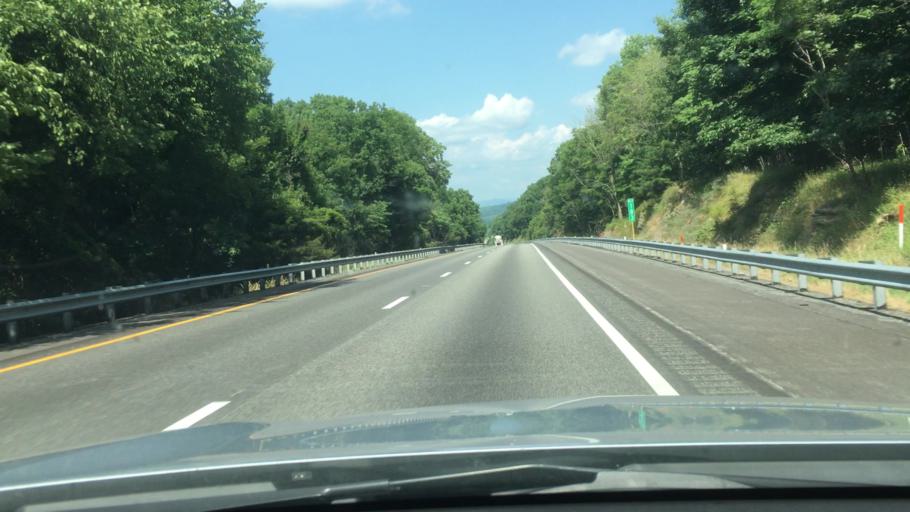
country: US
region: Virginia
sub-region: Rockbridge County
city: Glasgow
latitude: 37.6937
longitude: -79.4769
